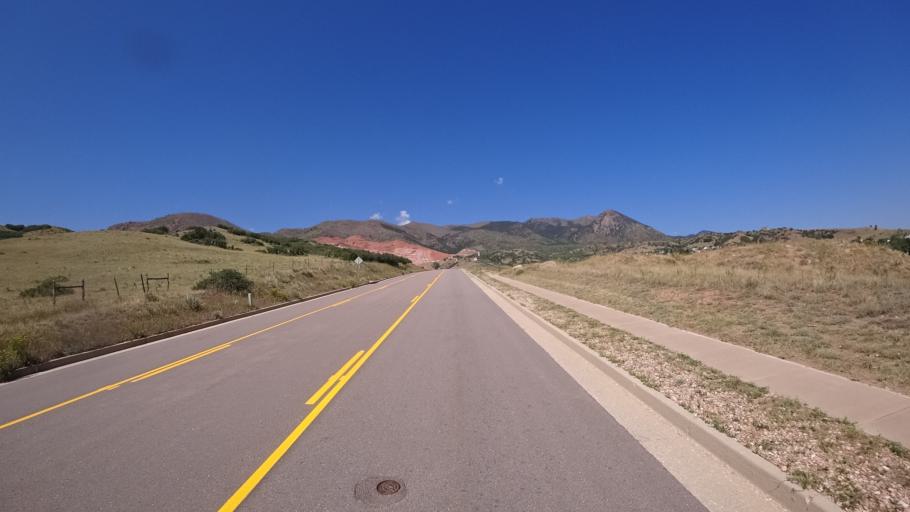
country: US
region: Colorado
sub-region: El Paso County
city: Air Force Academy
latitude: 38.9329
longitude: -104.8746
